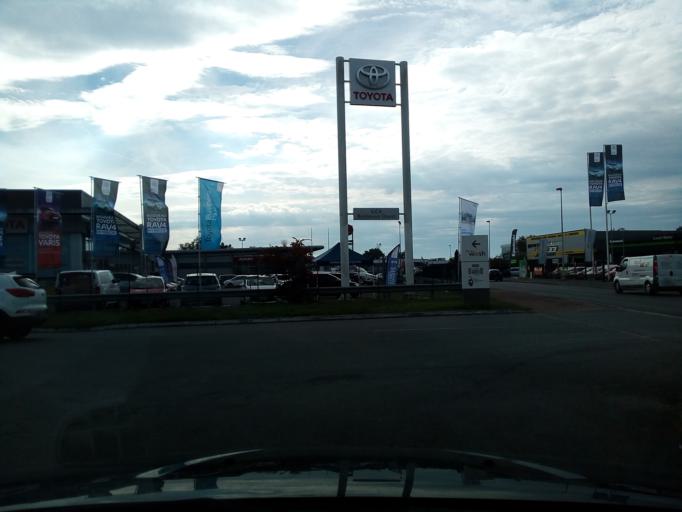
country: FR
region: Aquitaine
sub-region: Departement de la Gironde
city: Pessac
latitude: 44.8277
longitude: -0.6711
